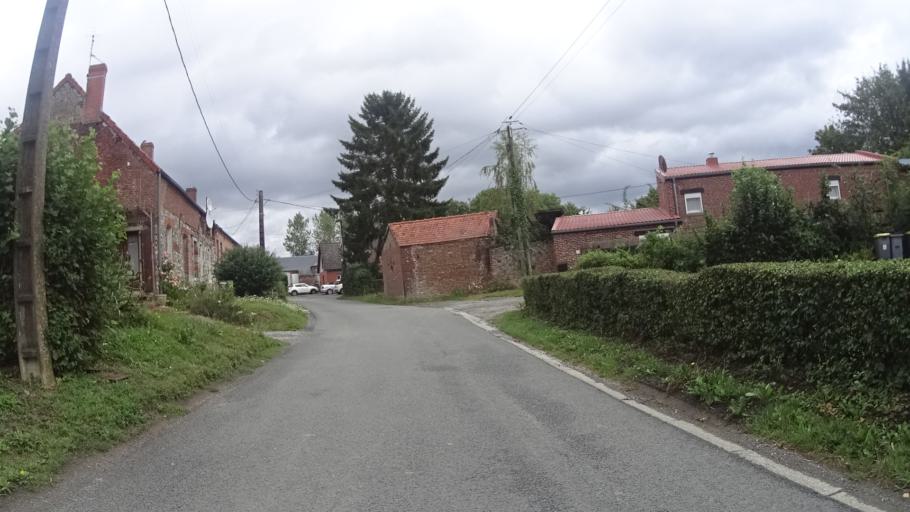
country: FR
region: Nord-Pas-de-Calais
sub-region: Departement du Nord
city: Berlaimont
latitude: 50.1773
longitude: 3.8023
